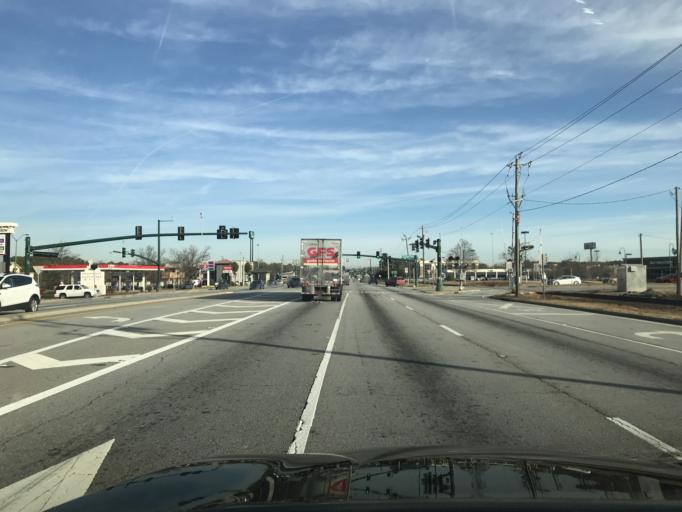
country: US
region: Georgia
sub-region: Clayton County
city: Morrow
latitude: 33.5729
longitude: -84.3422
